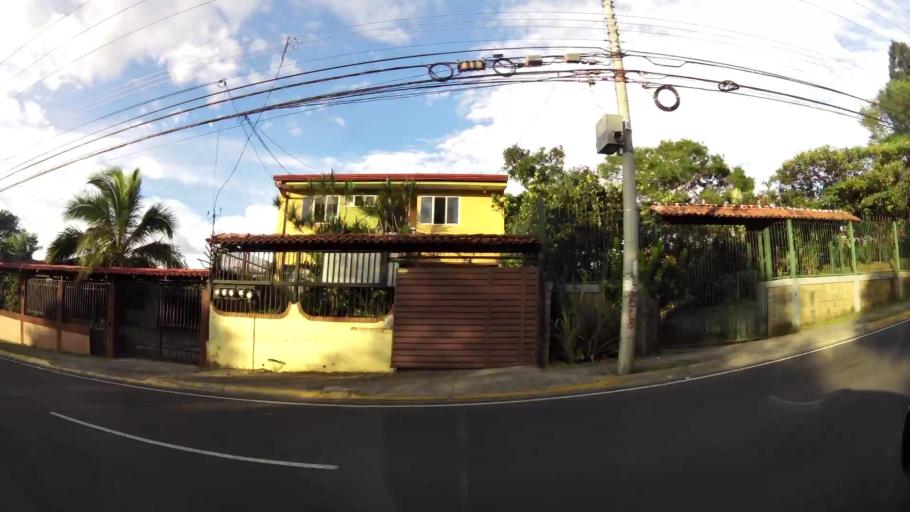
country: CR
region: Heredia
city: Mercedes
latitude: 9.9977
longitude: -84.1400
